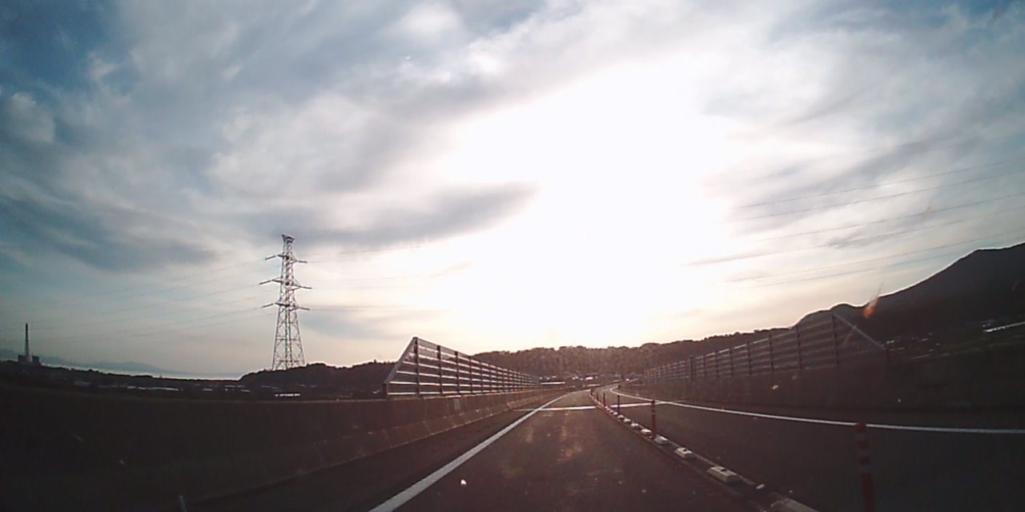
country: JP
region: Hokkaido
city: Date
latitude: 42.4982
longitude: 140.8580
